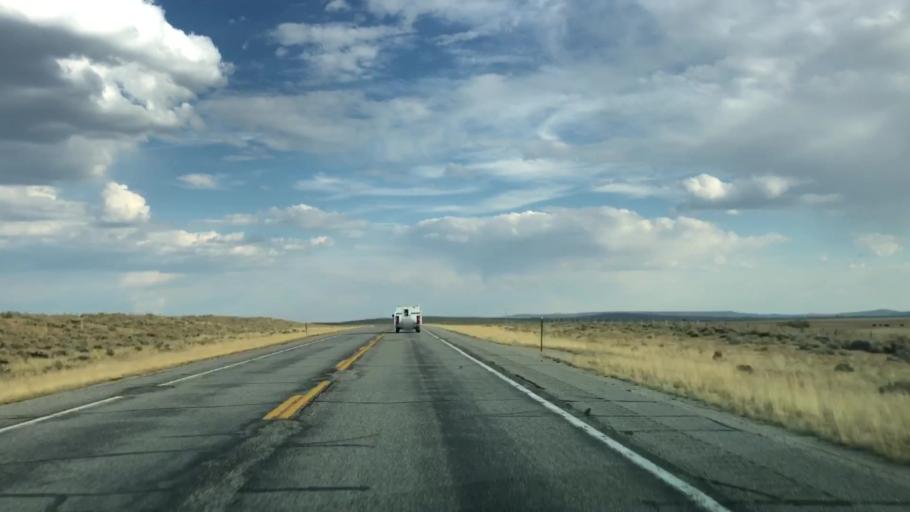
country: US
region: Wyoming
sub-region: Sublette County
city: Pinedale
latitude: 43.0385
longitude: -110.1367
